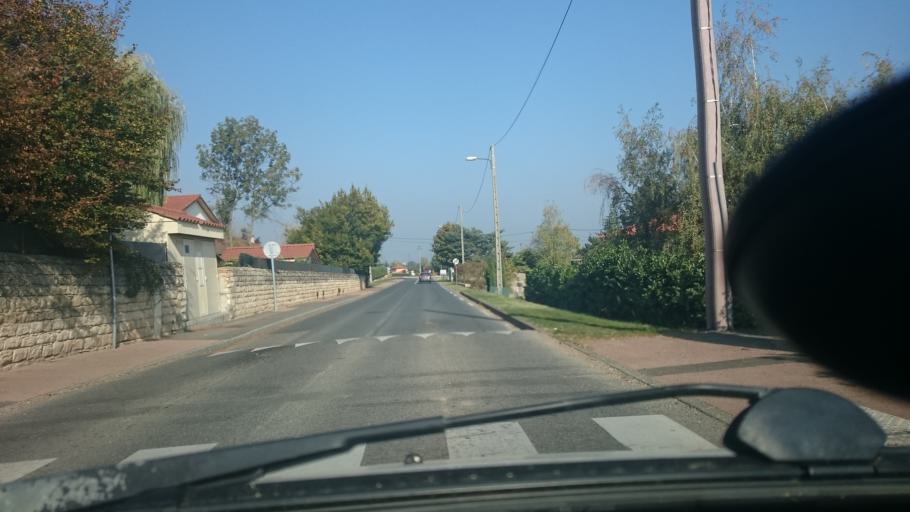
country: FR
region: Rhone-Alpes
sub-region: Departement du Rhone
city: Lucenay
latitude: 45.9158
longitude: 4.7046
